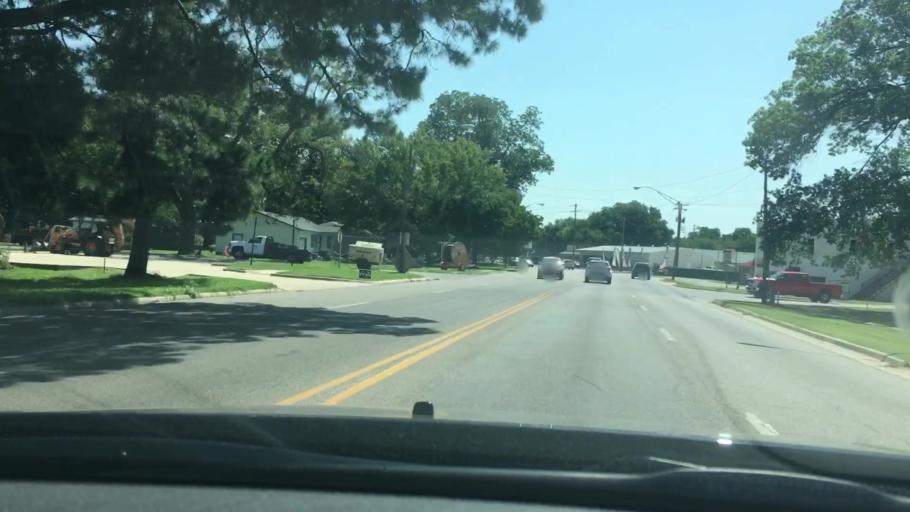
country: US
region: Oklahoma
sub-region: Johnston County
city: Tishomingo
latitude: 34.2314
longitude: -96.6716
